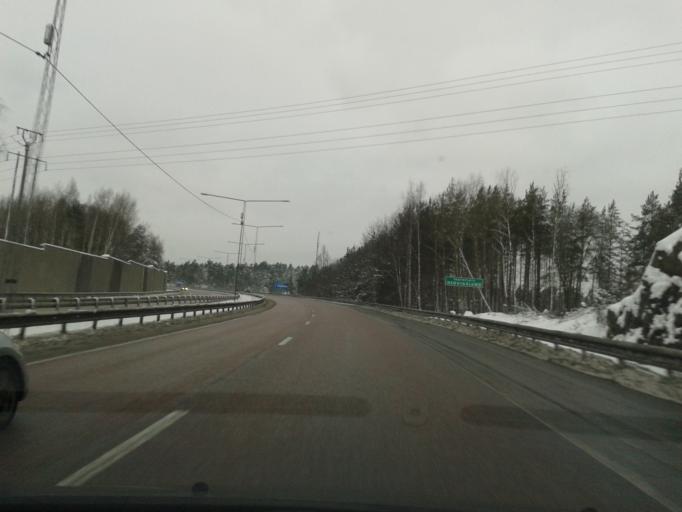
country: SE
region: Stockholm
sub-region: Tyreso Kommun
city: Bollmora
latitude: 59.2510
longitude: 18.2063
